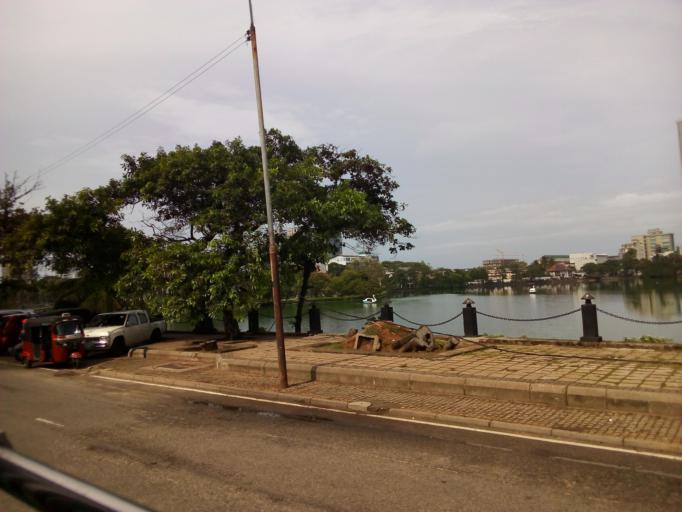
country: LK
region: Western
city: Colombo
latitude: 6.9193
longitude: 79.8539
